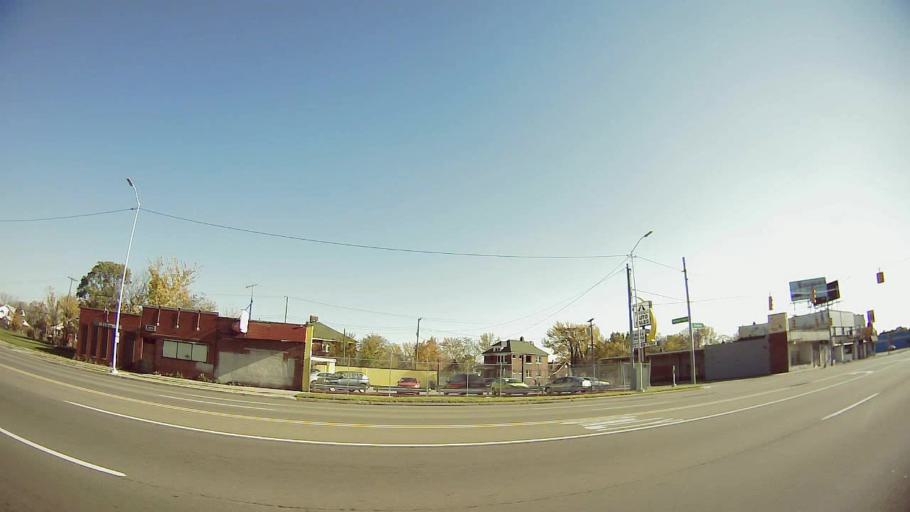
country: US
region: Michigan
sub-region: Macomb County
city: Eastpointe
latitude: 42.4250
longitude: -82.9845
